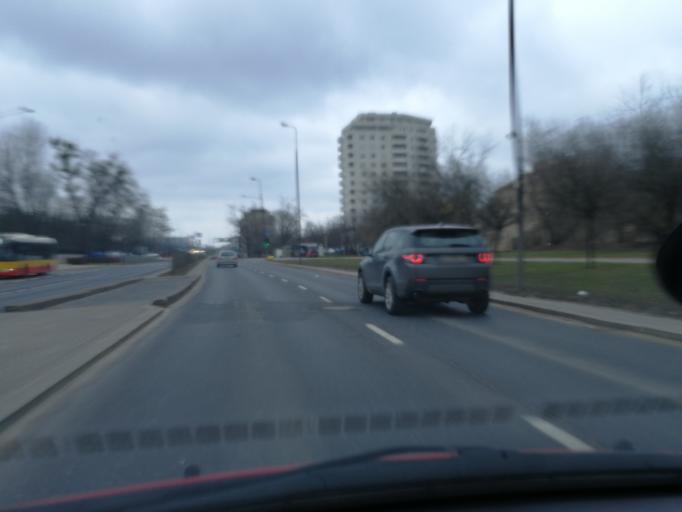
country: PL
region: Masovian Voivodeship
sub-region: Warszawa
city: Zoliborz
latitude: 52.2602
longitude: 20.9587
